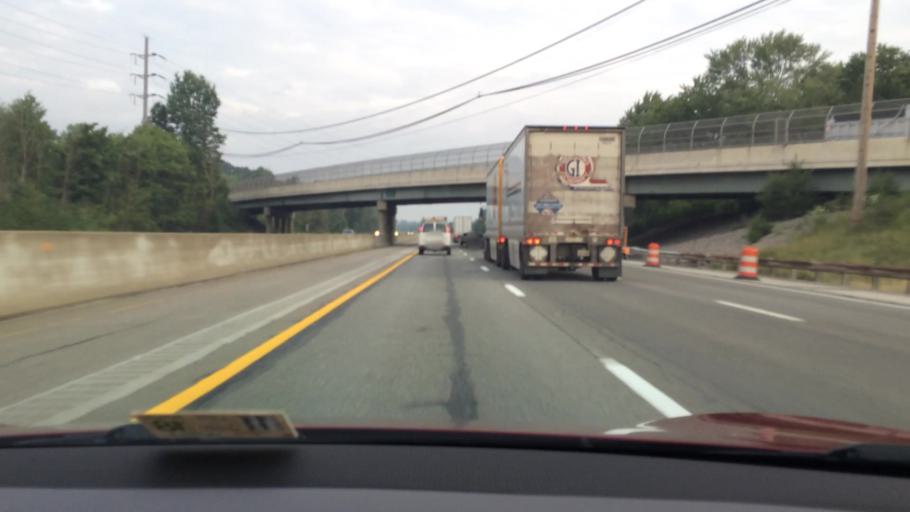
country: US
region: Ohio
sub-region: Cuyahoga County
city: Berea
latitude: 41.3502
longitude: -81.8650
